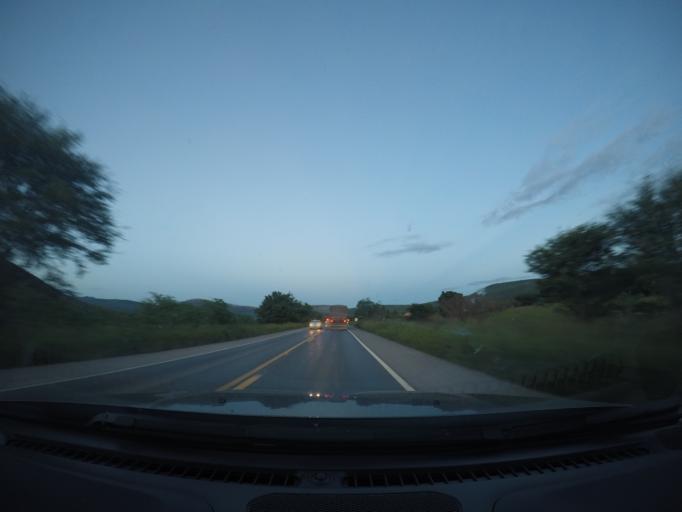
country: BR
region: Bahia
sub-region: Seabra
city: Seabra
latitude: -12.4865
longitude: -41.7259
